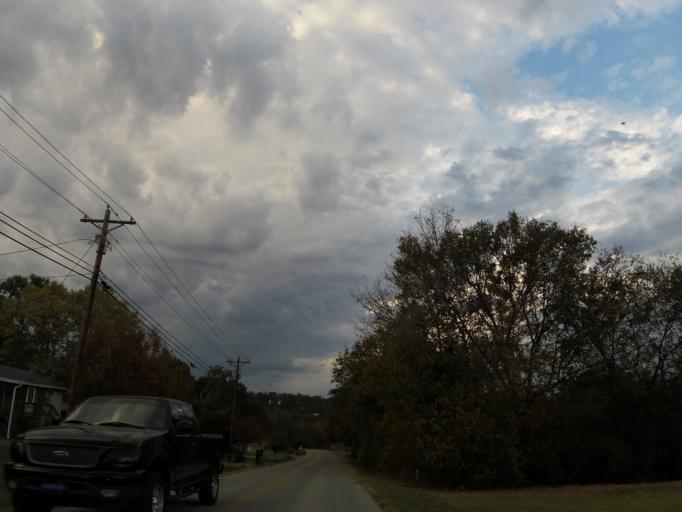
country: US
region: Tennessee
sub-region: Blount County
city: Louisville
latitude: 35.7755
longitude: -84.0488
